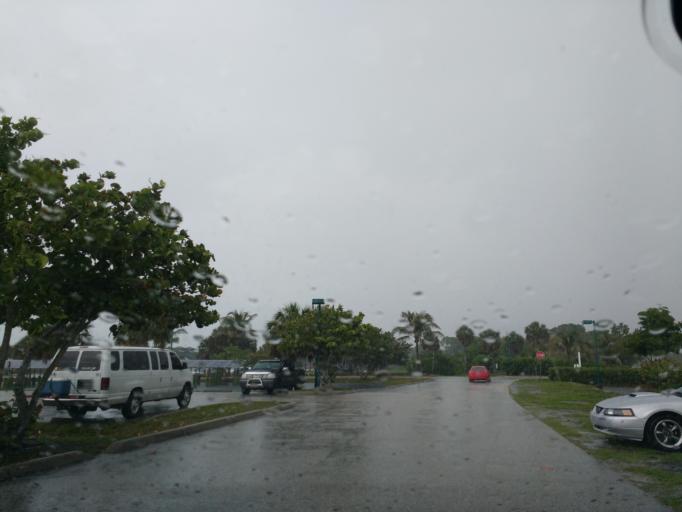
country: US
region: Florida
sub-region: Sarasota County
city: Venice
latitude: 27.0735
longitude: -82.4496
